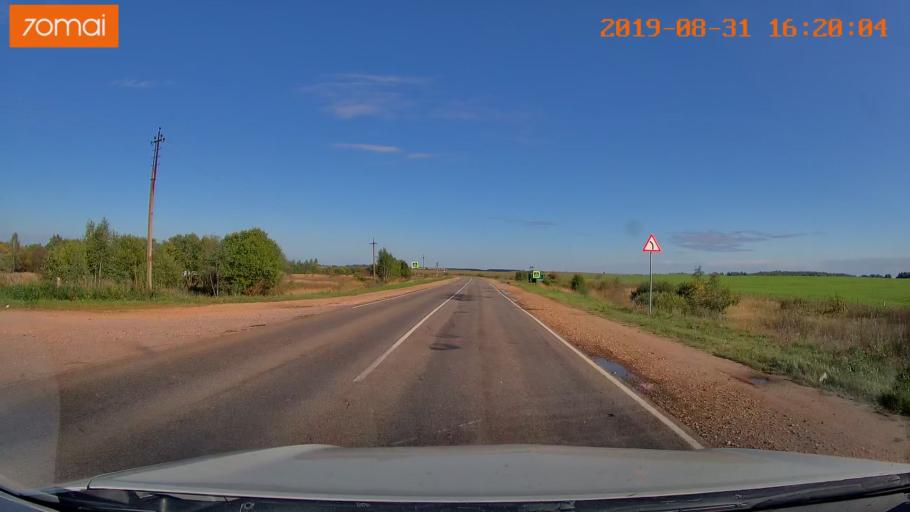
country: RU
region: Kaluga
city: Babynino
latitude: 54.5244
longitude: 35.5948
